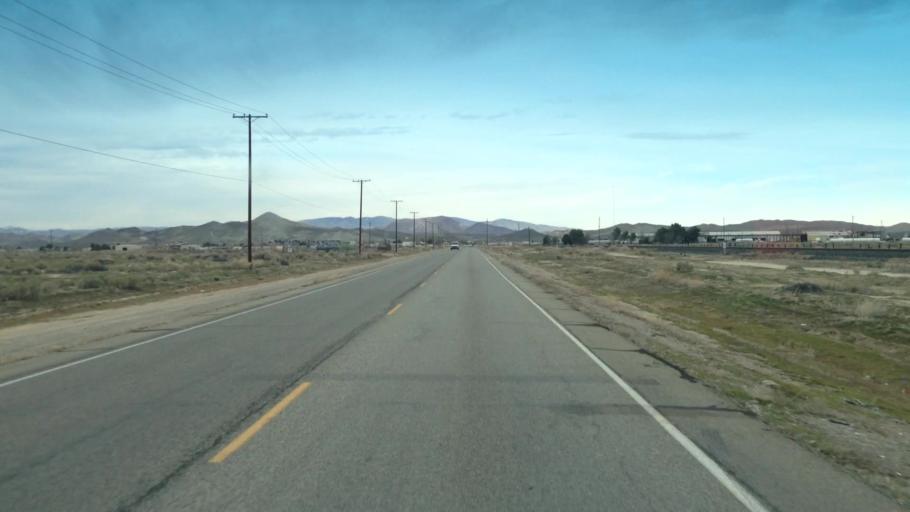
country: US
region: California
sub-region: Kern County
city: Rosamond
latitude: 34.8291
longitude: -118.1574
